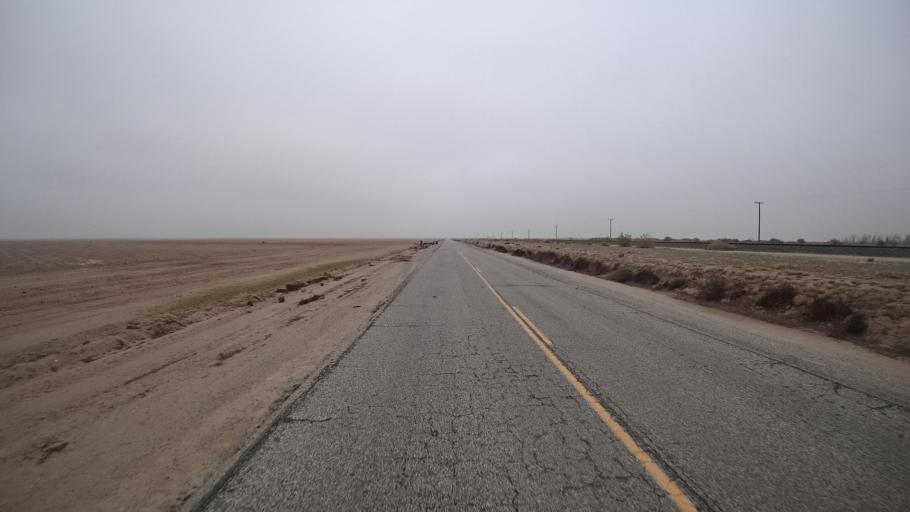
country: US
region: California
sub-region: Kern County
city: Maricopa
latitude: 35.1254
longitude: -119.2626
